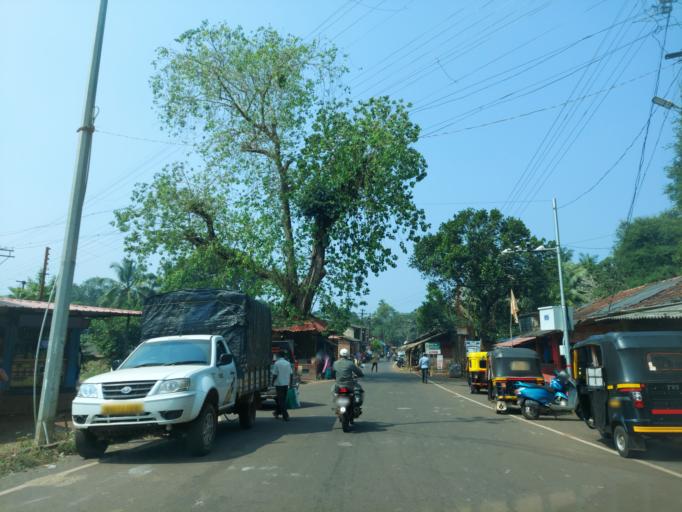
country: IN
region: Maharashtra
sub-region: Sindhudurg
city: Malvan
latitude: 15.9889
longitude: 73.5265
